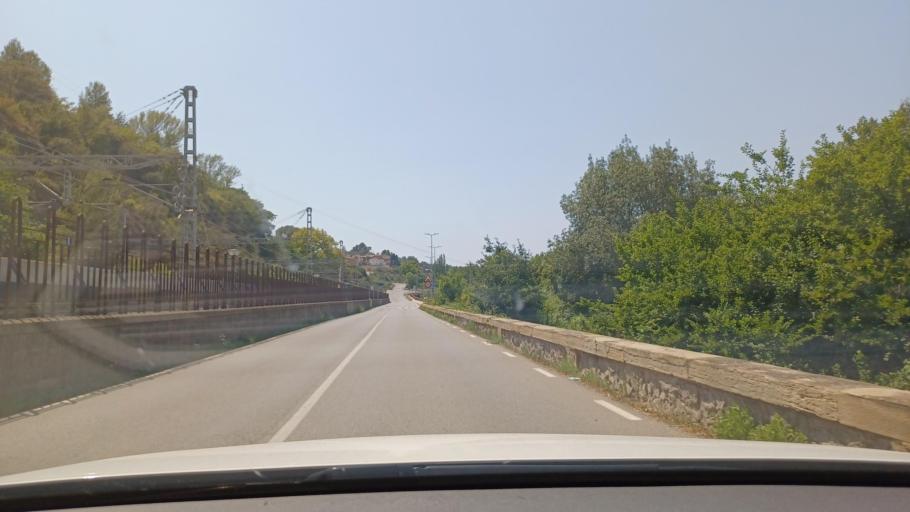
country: ES
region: Catalonia
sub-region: Provincia de Barcelona
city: Manresa
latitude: 41.7204
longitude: 1.8242
